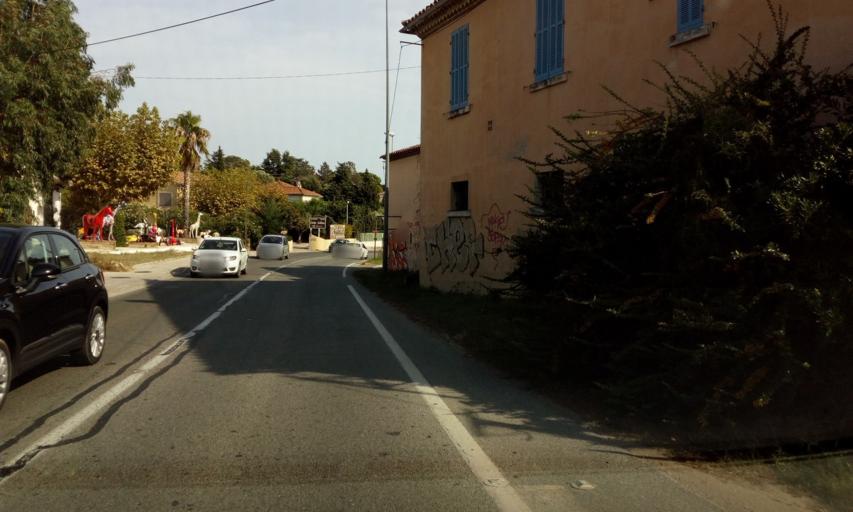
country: FR
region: Provence-Alpes-Cote d'Azur
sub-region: Departement du Var
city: Bormes-les-Mimosas
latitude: 43.1415
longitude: 6.3491
